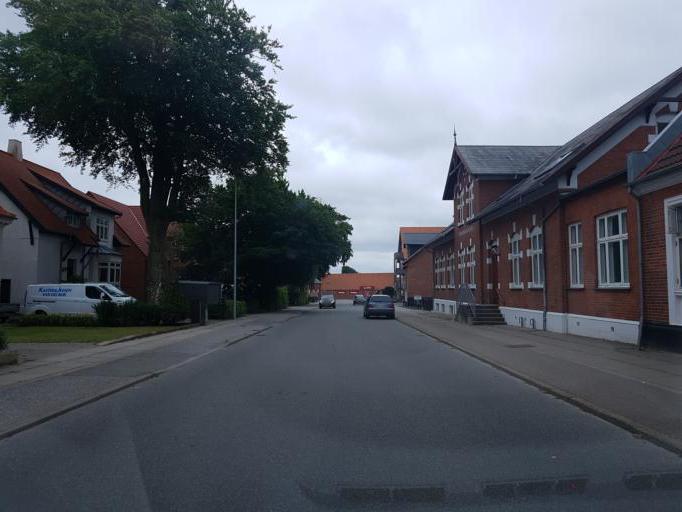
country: DK
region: South Denmark
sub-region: Varde Kommune
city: Varde
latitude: 55.6247
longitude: 8.4848
